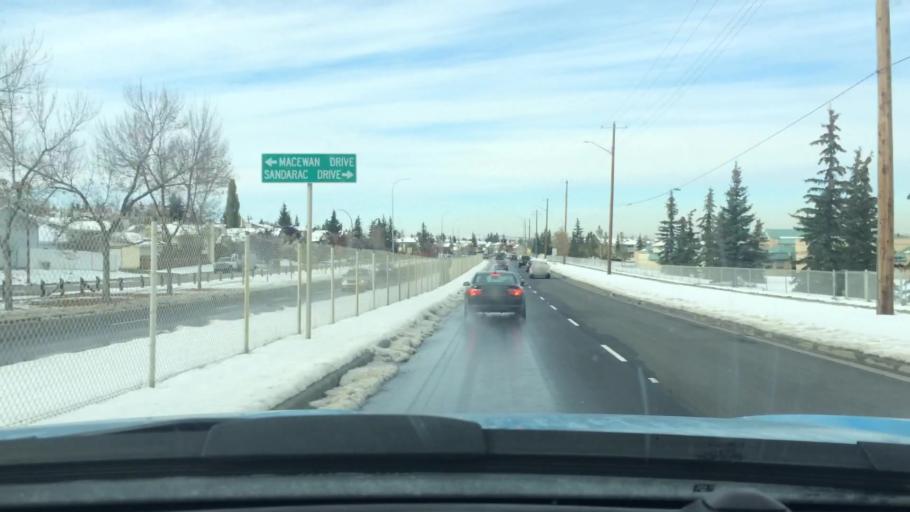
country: CA
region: Alberta
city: Calgary
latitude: 51.1375
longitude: -114.1079
